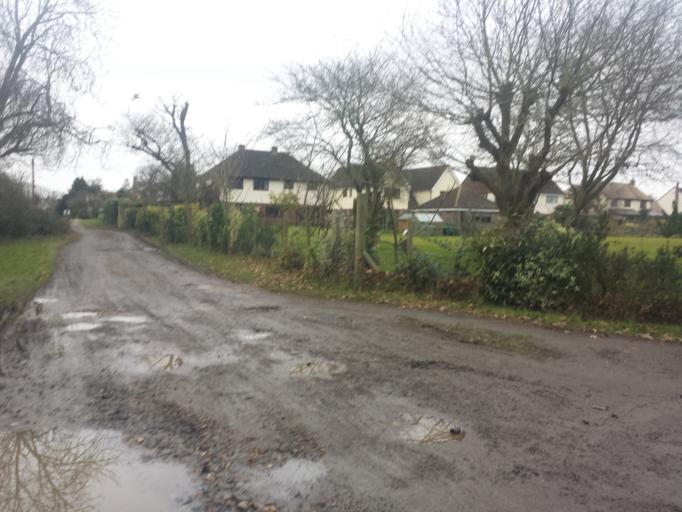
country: GB
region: England
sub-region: Essex
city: Little Clacton
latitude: 51.8622
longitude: 1.1597
